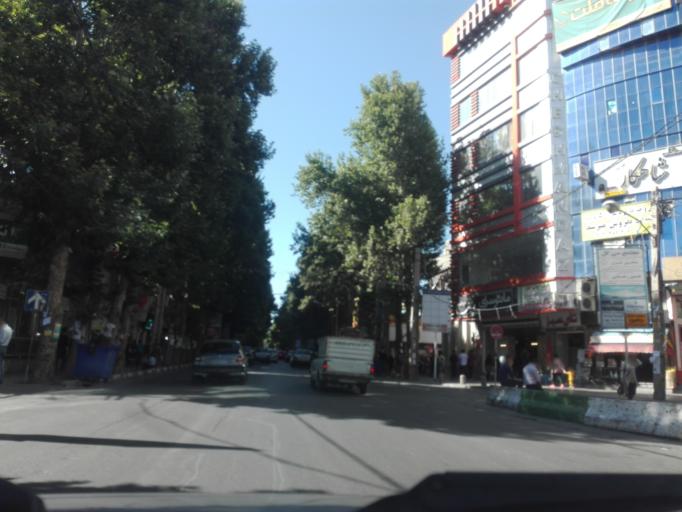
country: IR
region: Tehran
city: Shahriar
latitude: 35.6548
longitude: 51.0595
